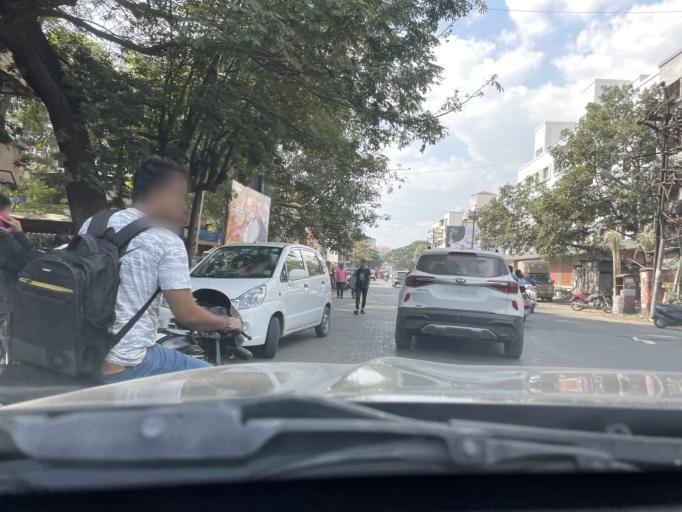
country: IN
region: Maharashtra
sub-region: Pune Division
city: Pune
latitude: 18.4814
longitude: 73.9007
